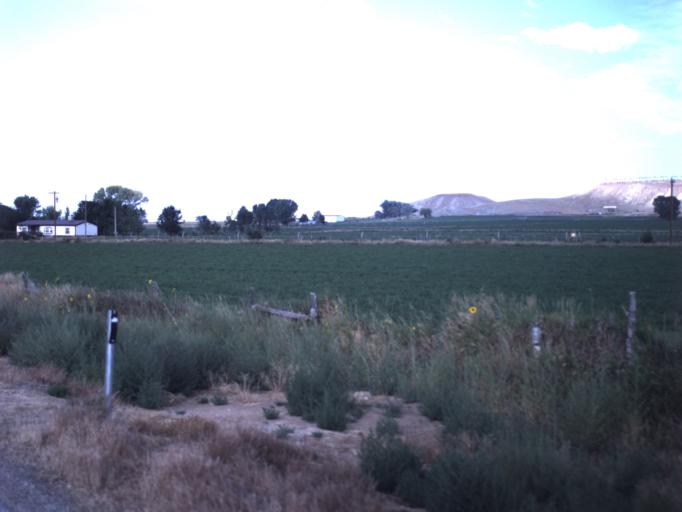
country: US
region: Utah
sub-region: Uintah County
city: Naples
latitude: 40.4021
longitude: -109.3446
